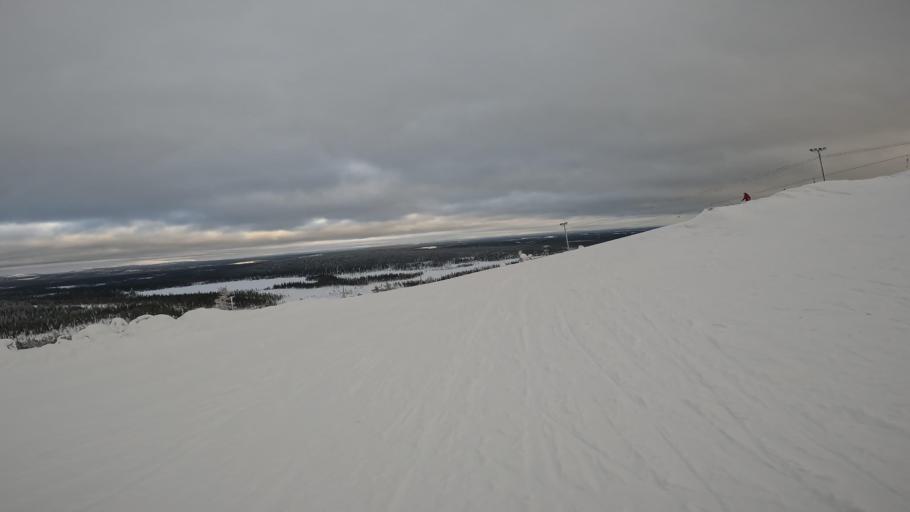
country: FI
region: Lapland
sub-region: Itae-Lappi
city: Salla
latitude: 66.7637
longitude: 28.7894
